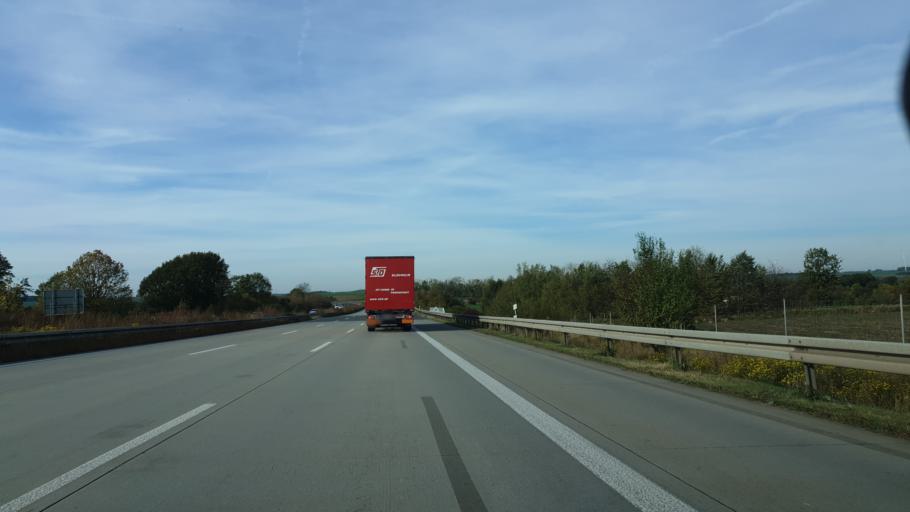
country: DE
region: Thuringia
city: Ponitz
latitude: 50.8293
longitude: 12.4206
